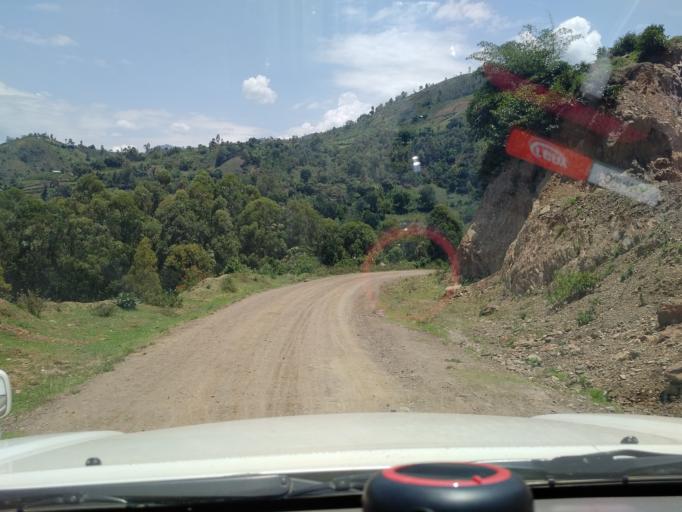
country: CD
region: Nord Kivu
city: Sake
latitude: -1.7937
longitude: 29.0085
